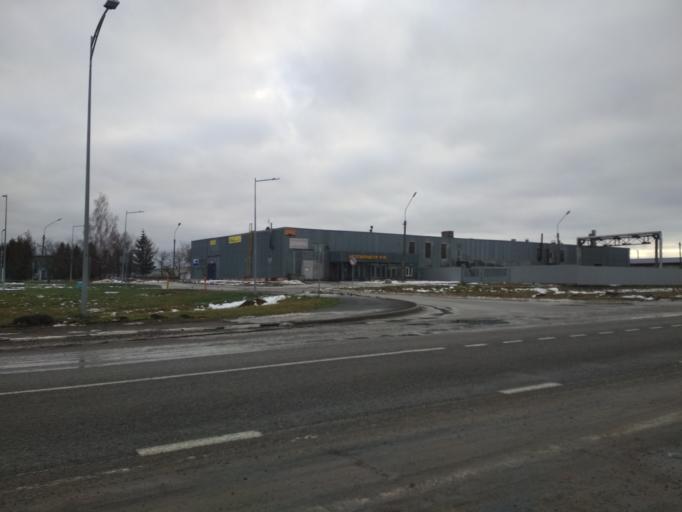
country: BY
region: Minsk
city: Mar''ina Horka
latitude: 53.5097
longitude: 28.1074
